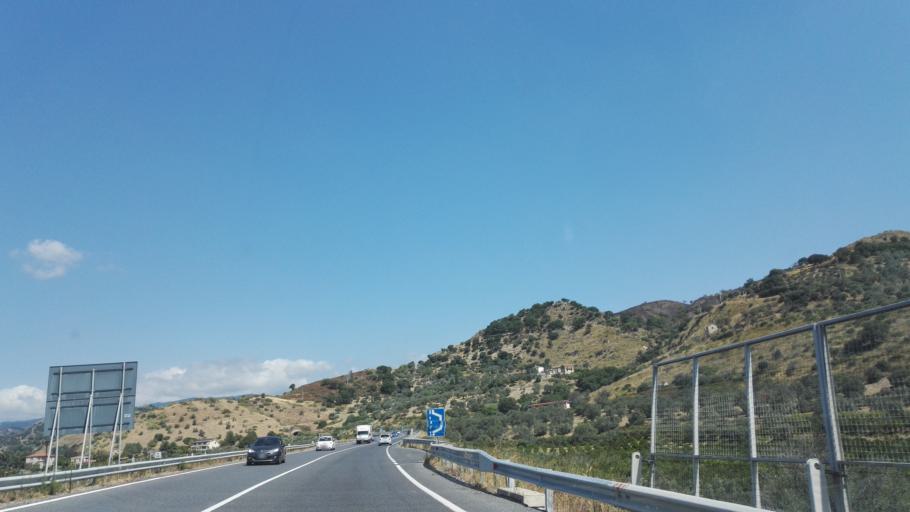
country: IT
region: Calabria
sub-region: Provincia di Reggio Calabria
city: Gioiosa Ionica
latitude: 38.3281
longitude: 16.2919
